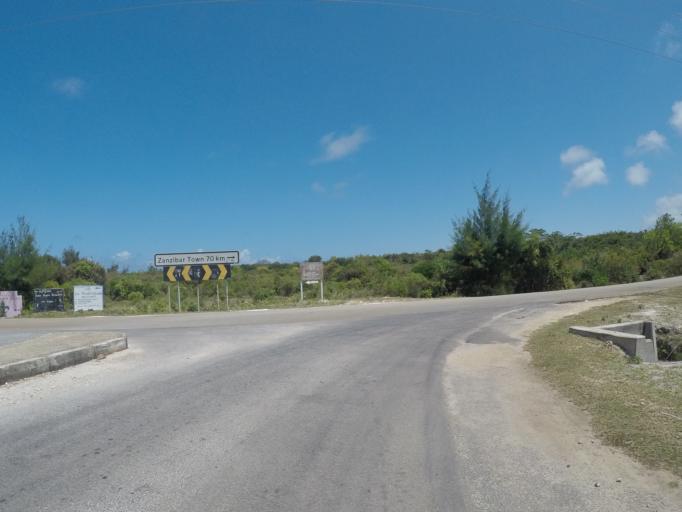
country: TZ
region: Zanzibar Central/South
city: Nganane
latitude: -6.4104
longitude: 39.5641
